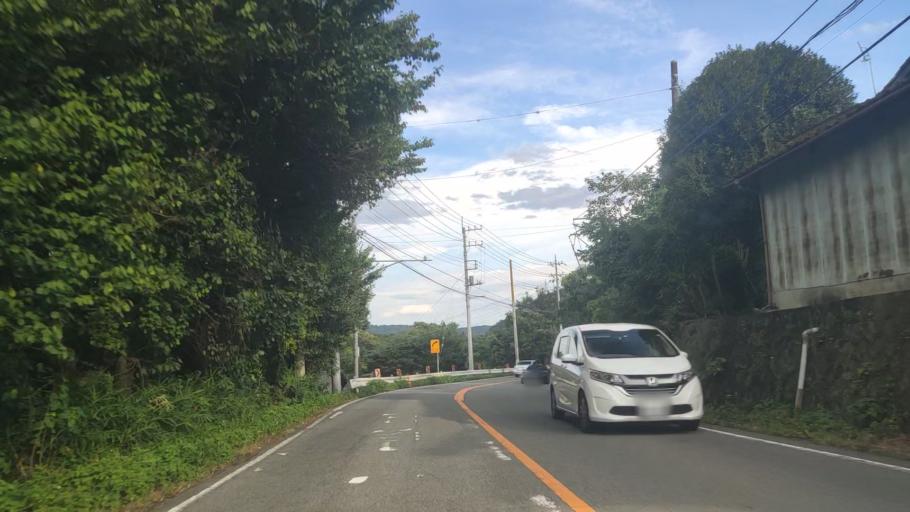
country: JP
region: Gunma
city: Omamacho-omama
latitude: 36.4592
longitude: 139.2635
